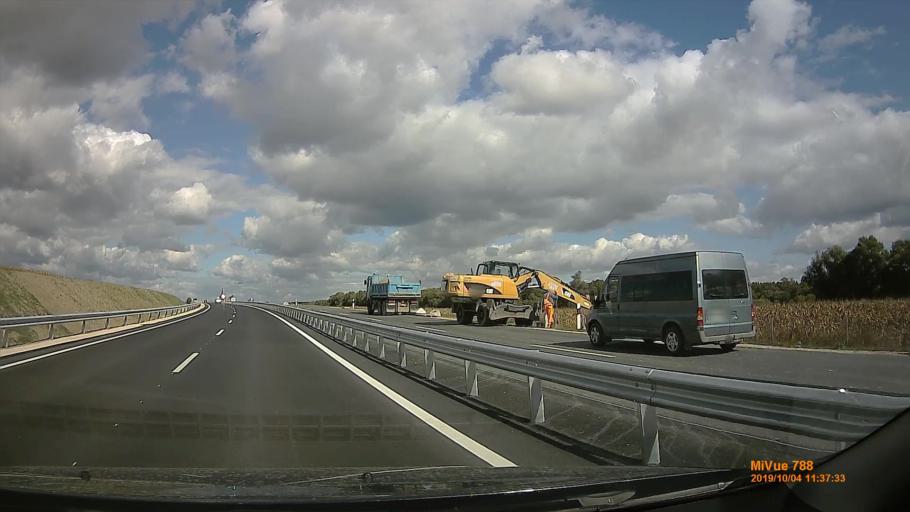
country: HU
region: Somogy
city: Karad
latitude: 46.5372
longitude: 17.8169
